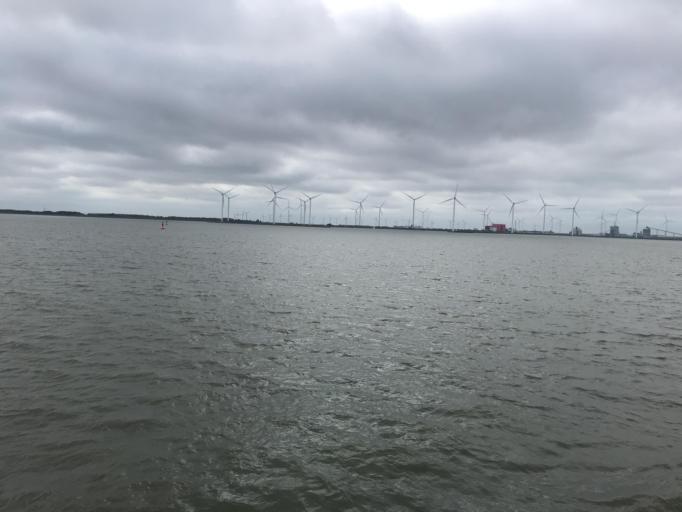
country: NL
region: Groningen
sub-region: Gemeente Delfzijl
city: Delfzijl
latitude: 53.3281
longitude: 7.0217
